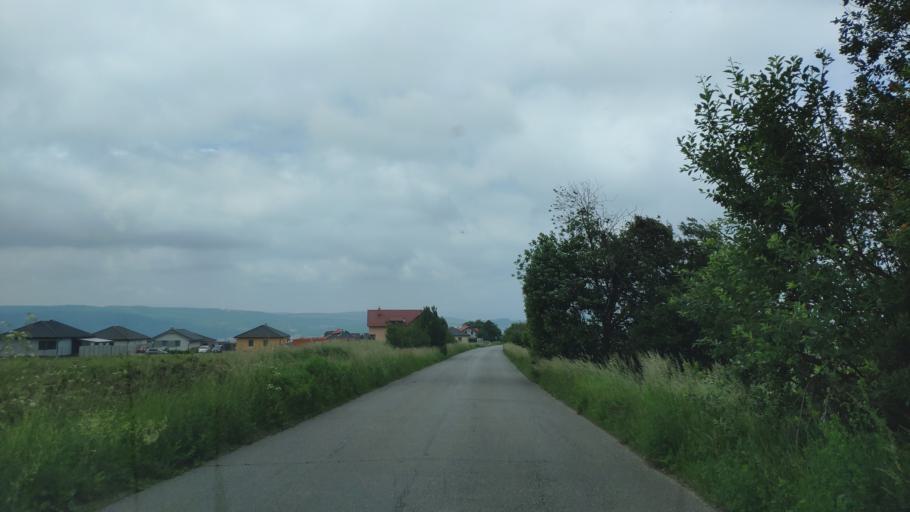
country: SK
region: Presovsky
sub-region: Okres Presov
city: Presov
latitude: 48.9970
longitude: 21.2950
